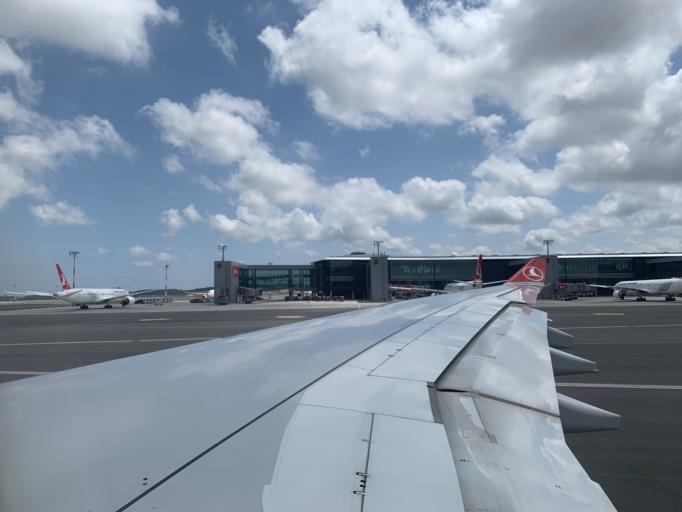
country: TR
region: Istanbul
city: Durusu
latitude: 41.2676
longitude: 28.7389
